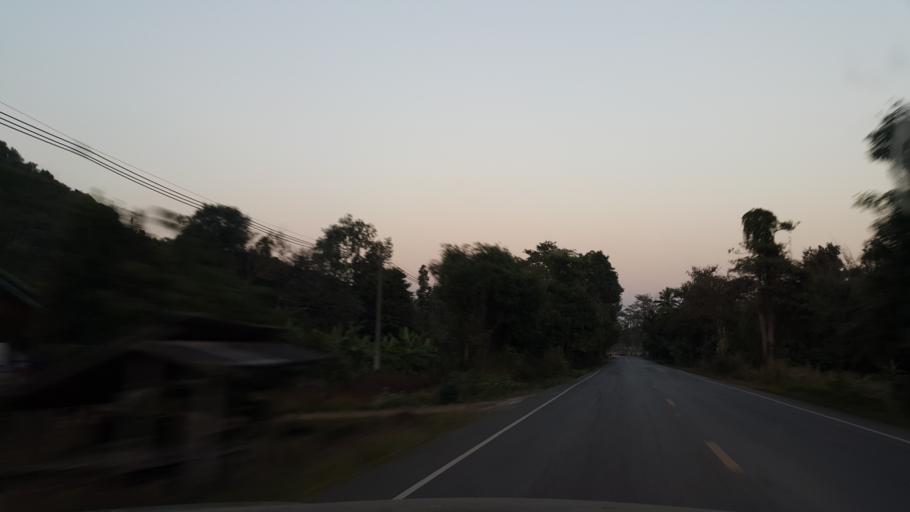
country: TH
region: Phrae
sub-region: Amphoe Wang Chin
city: Wang Chin
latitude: 17.9743
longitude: 99.6325
